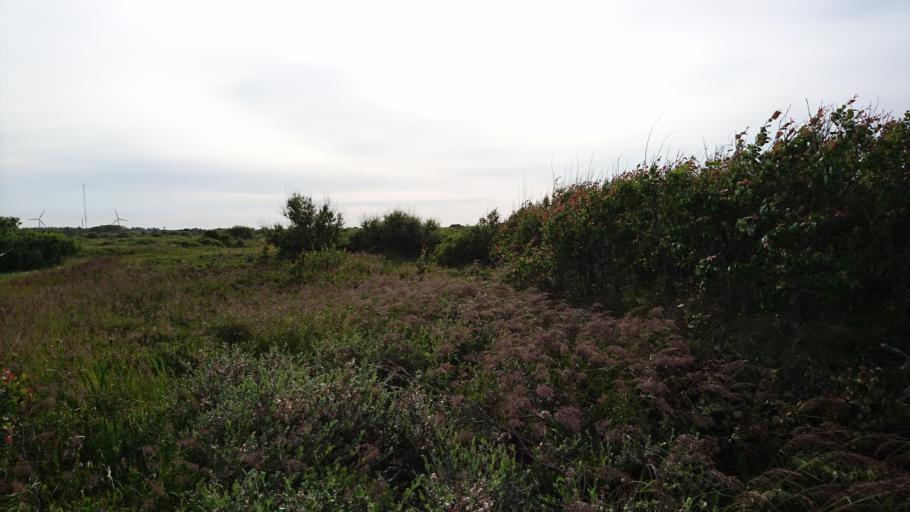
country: DK
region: North Denmark
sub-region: Frederikshavn Kommune
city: Skagen
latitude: 57.7432
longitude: 10.5936
